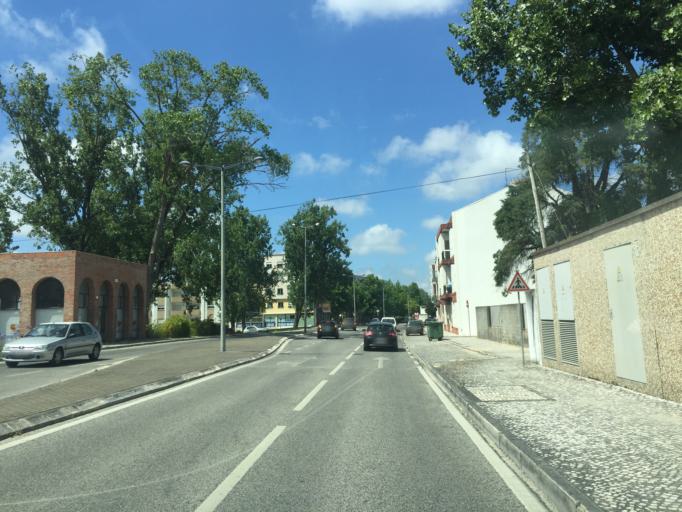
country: PT
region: Leiria
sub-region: Marinha Grande
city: Marinha Grande
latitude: 39.7430
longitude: -8.9355
